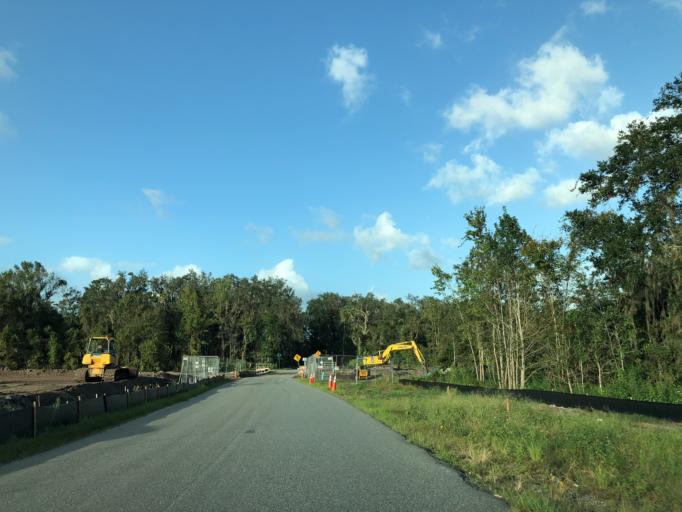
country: US
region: Florida
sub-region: Seminole County
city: Winter Springs
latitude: 28.6960
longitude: -81.2588
